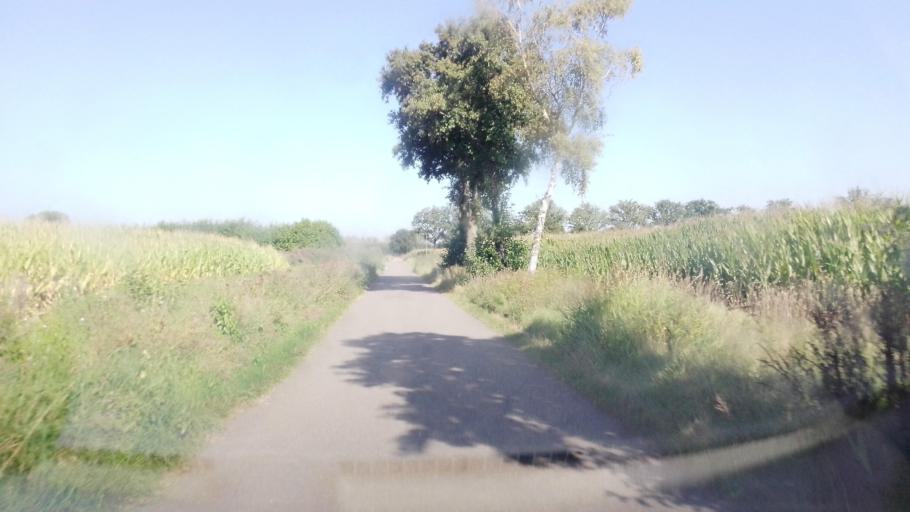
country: NL
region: Limburg
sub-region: Gemeente Peel en Maas
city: Maasbree
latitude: 51.3643
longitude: 6.0087
